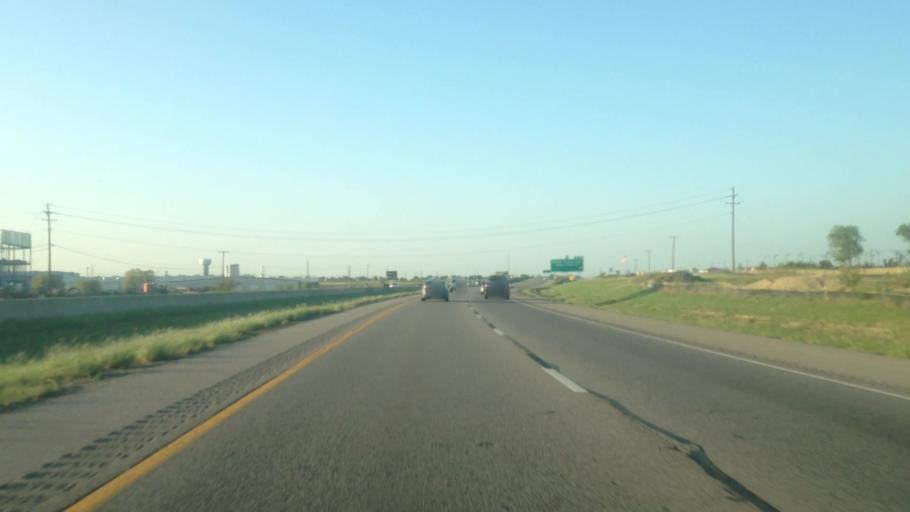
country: US
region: Texas
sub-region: Tarrant County
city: Haslet
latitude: 32.9274
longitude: -97.3170
